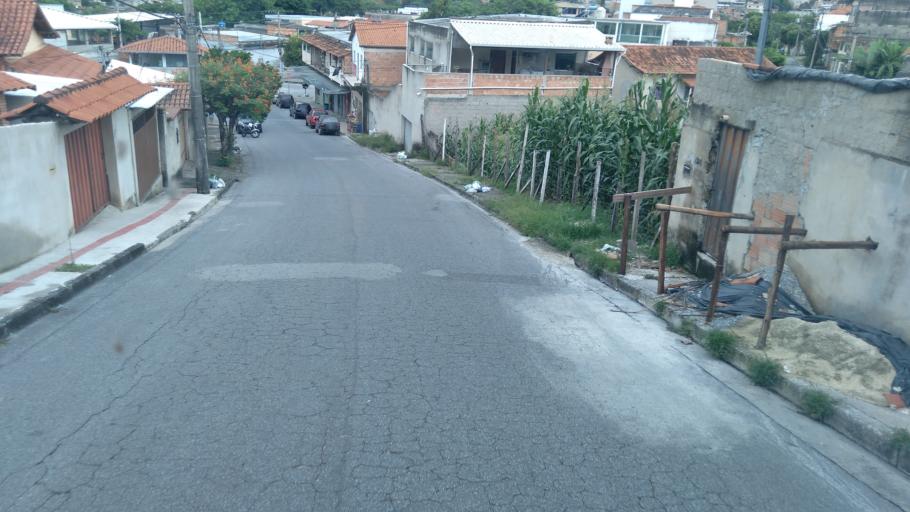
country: BR
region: Minas Gerais
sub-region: Belo Horizonte
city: Belo Horizonte
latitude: -19.8461
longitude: -43.9081
